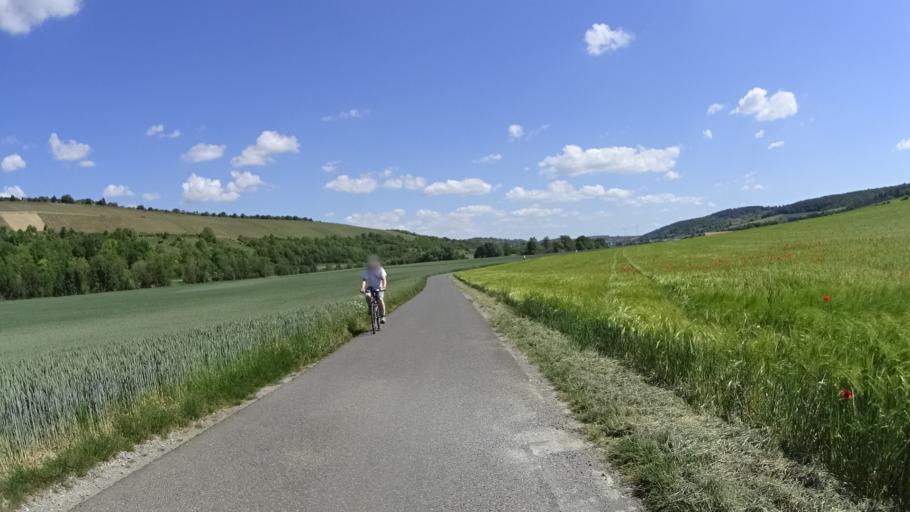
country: DE
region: Bavaria
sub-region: Regierungsbezirk Unterfranken
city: Tauberrettersheim
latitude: 49.4969
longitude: 9.9532
